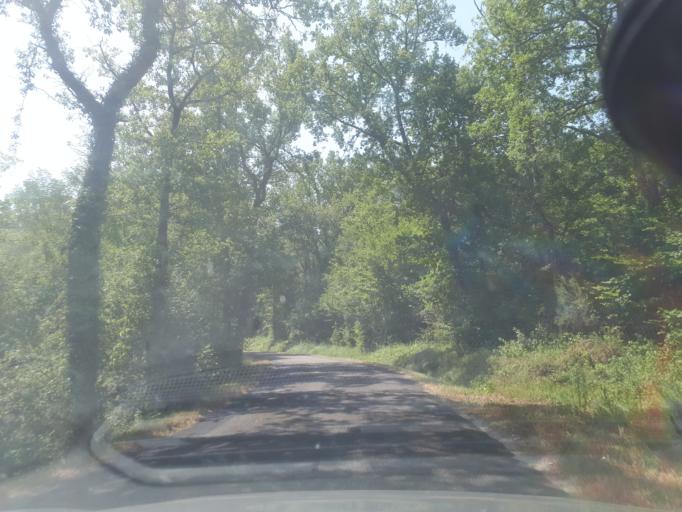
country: FR
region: Midi-Pyrenees
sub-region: Departement du Lot
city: Souillac
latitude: 44.8414
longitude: 1.3997
